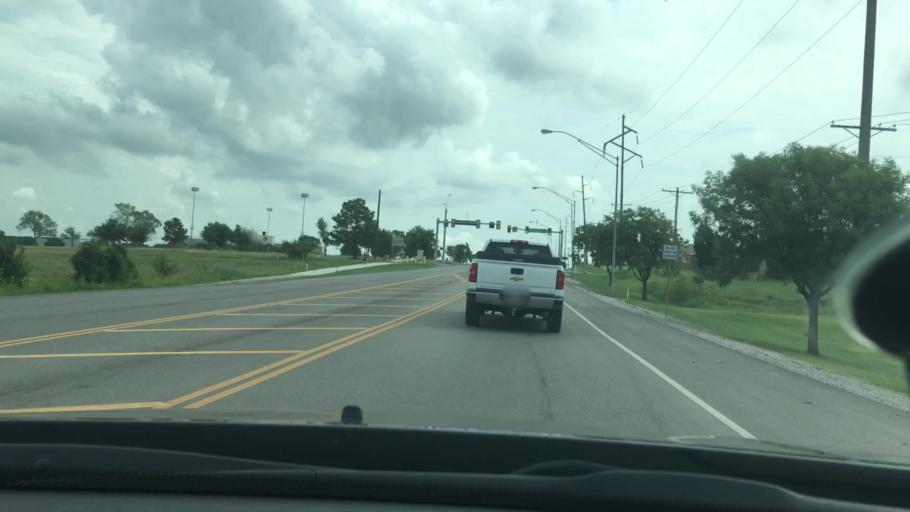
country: US
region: Oklahoma
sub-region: Carter County
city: Ardmore
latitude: 34.2029
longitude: -97.1421
